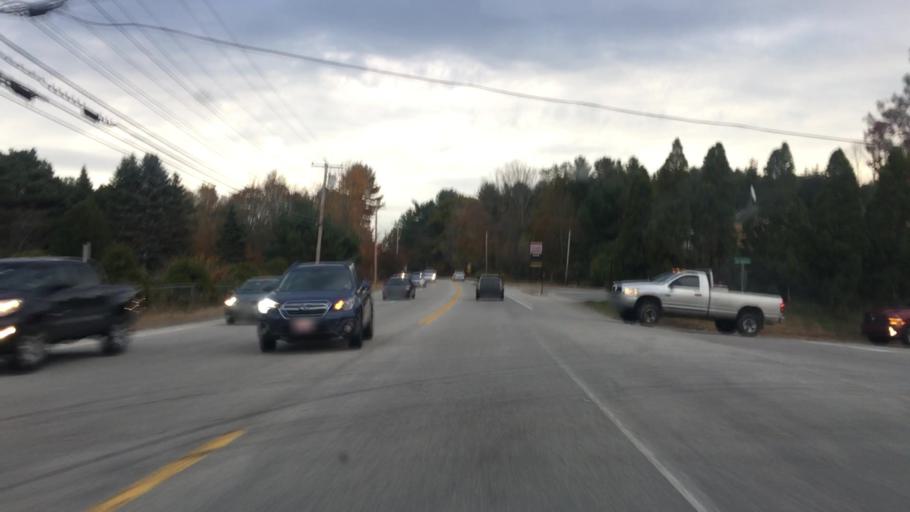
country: US
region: Maine
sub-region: York County
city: Biddeford
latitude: 43.4740
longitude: -70.5277
